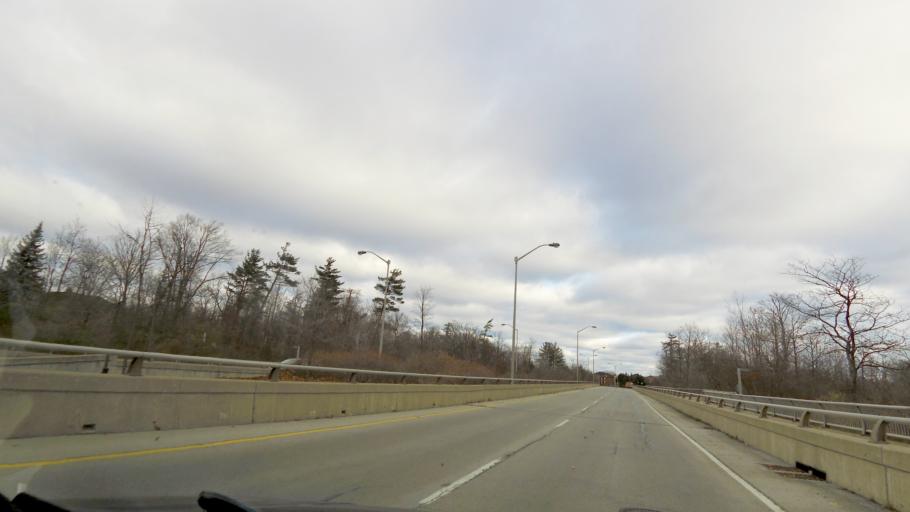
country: CA
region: Ontario
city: Oakville
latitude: 43.4610
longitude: -79.7257
